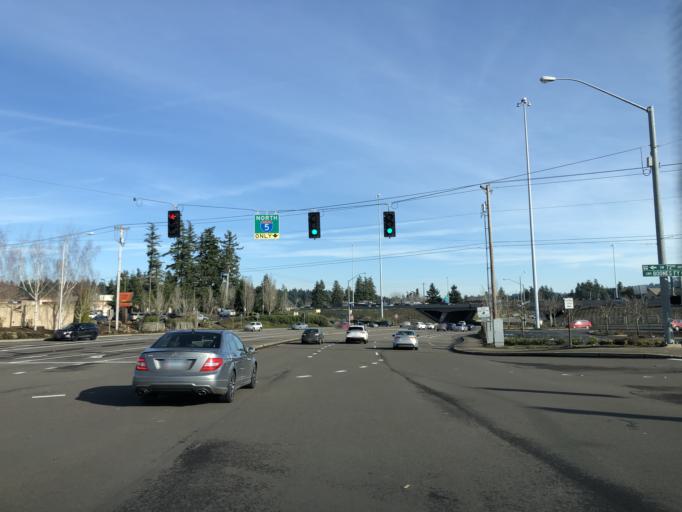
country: US
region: Oregon
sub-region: Washington County
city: Durham
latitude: 45.3958
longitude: -122.7500
